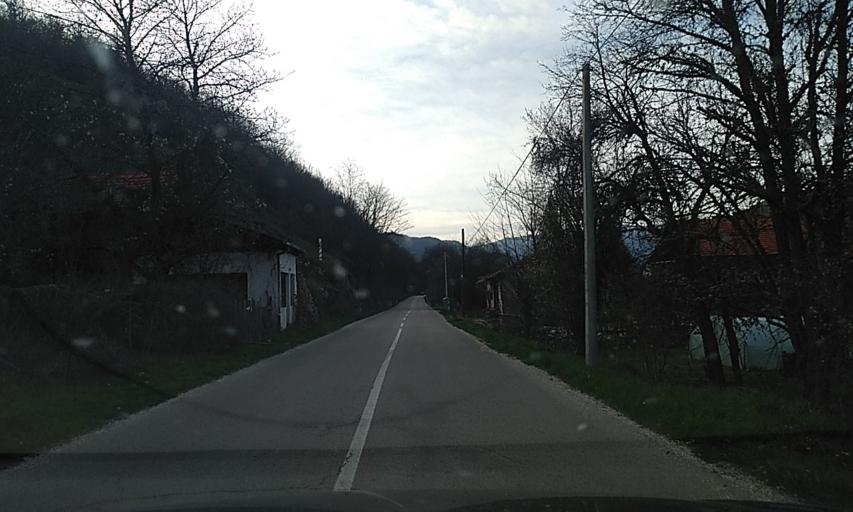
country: RS
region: Central Serbia
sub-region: Pcinjski Okrug
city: Bosilegrad
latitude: 42.4557
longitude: 22.4951
